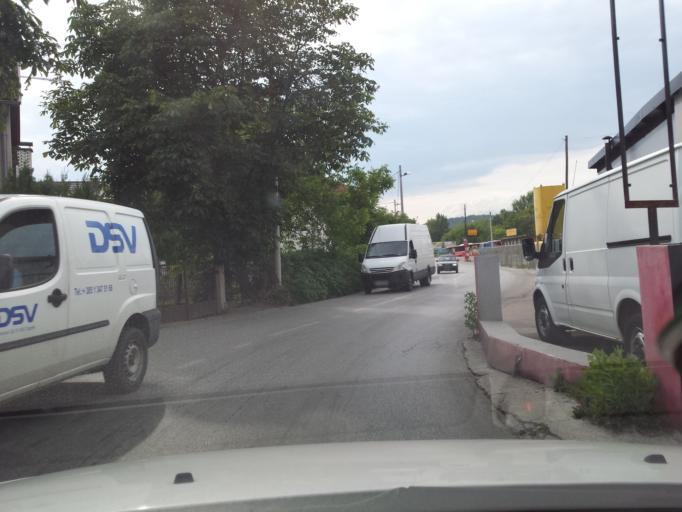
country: HR
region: Grad Zagreb
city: Jankomir
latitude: 45.8084
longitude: 15.9340
